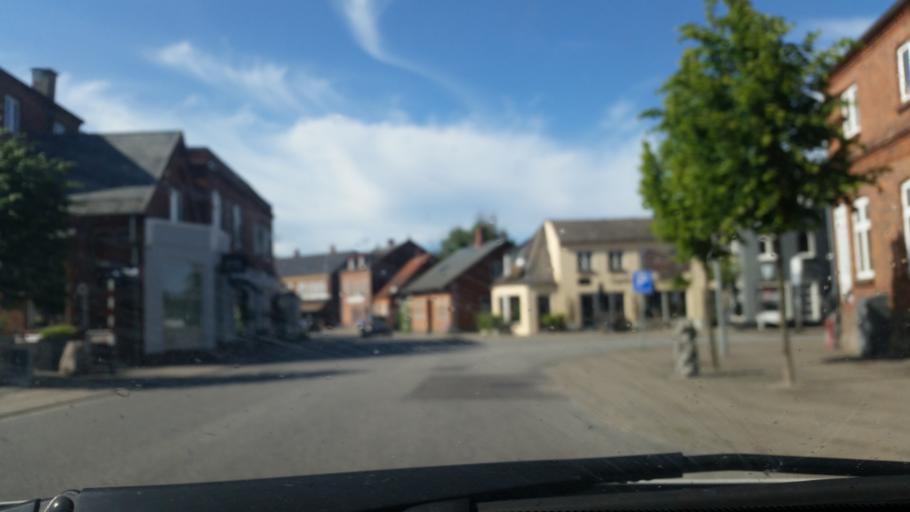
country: DK
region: Central Jutland
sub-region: Samso Kommune
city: Tranebjerg
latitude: 55.8320
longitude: 10.5946
